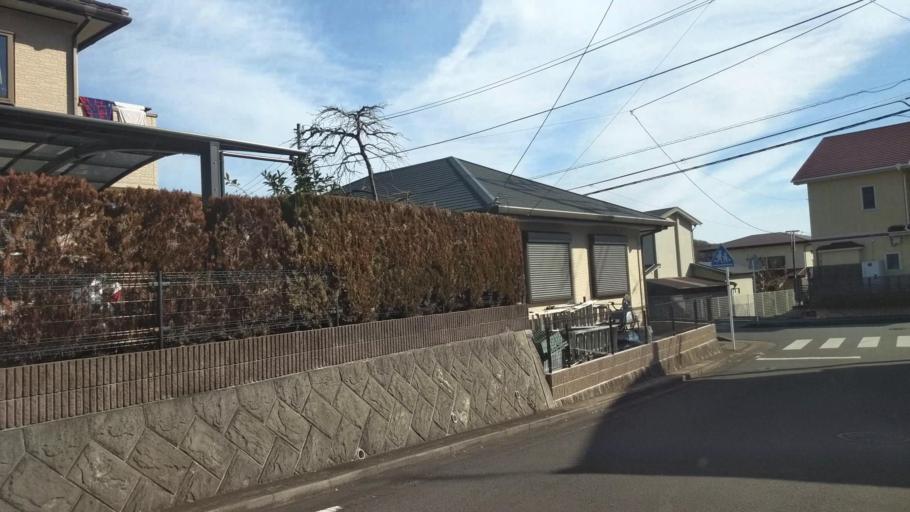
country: JP
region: Kanagawa
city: Hadano
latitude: 35.3592
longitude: 139.2328
